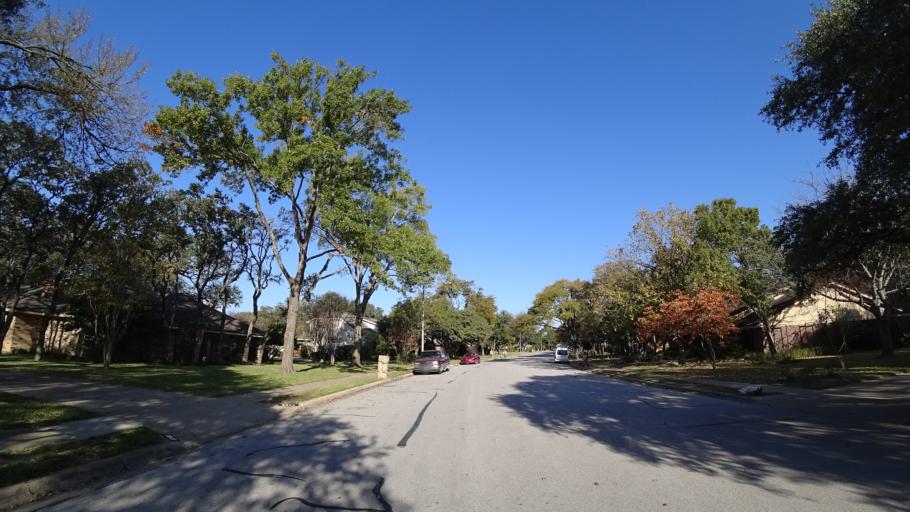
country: US
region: Texas
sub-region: Travis County
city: Shady Hollow
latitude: 30.2205
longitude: -97.8450
